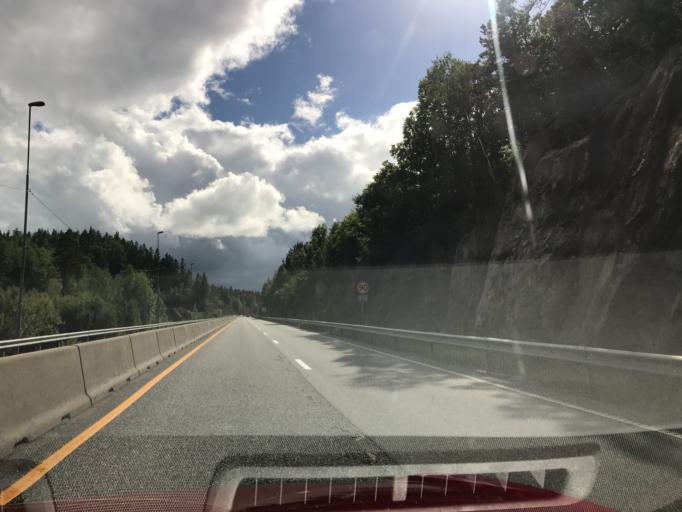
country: NO
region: Aust-Agder
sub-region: Gjerstad
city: Gjerstad
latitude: 58.8319
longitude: 9.0870
